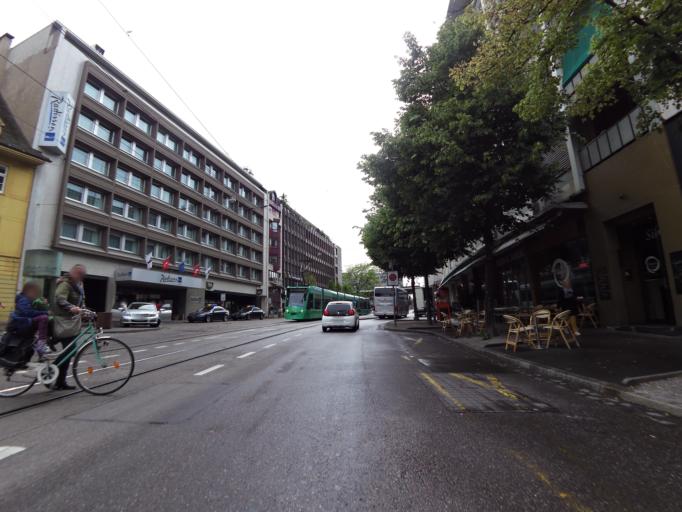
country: CH
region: Basel-City
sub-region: Basel-Stadt
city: Basel
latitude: 47.5516
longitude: 7.5891
